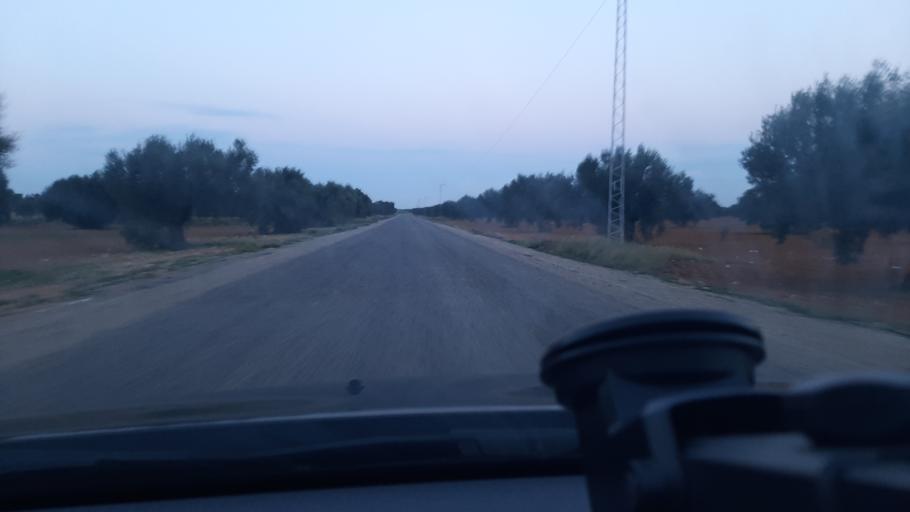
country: TN
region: Al Mahdiyah
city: Shurban
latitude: 35.0249
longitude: 10.4731
